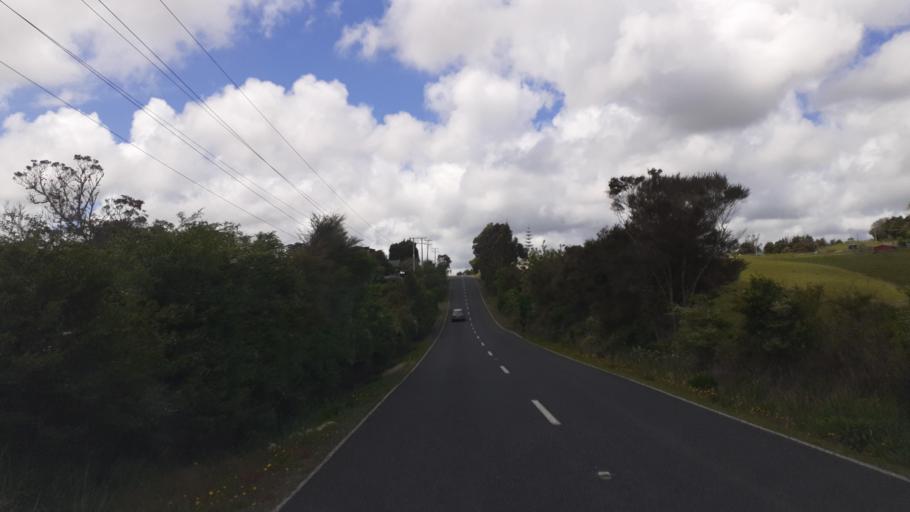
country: NZ
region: Northland
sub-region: Far North District
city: Kawakawa
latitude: -35.3641
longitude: 174.0926
